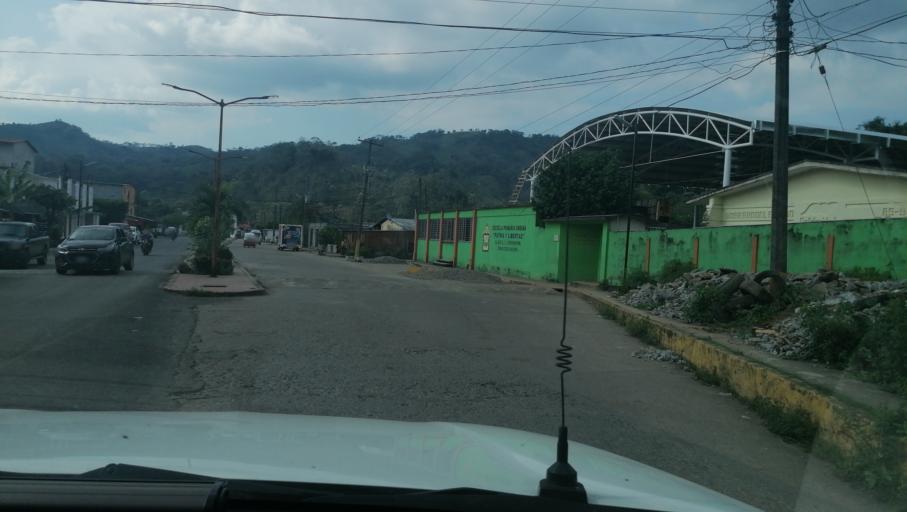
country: MX
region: Chiapas
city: Ostuacan
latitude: 17.4132
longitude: -93.3360
